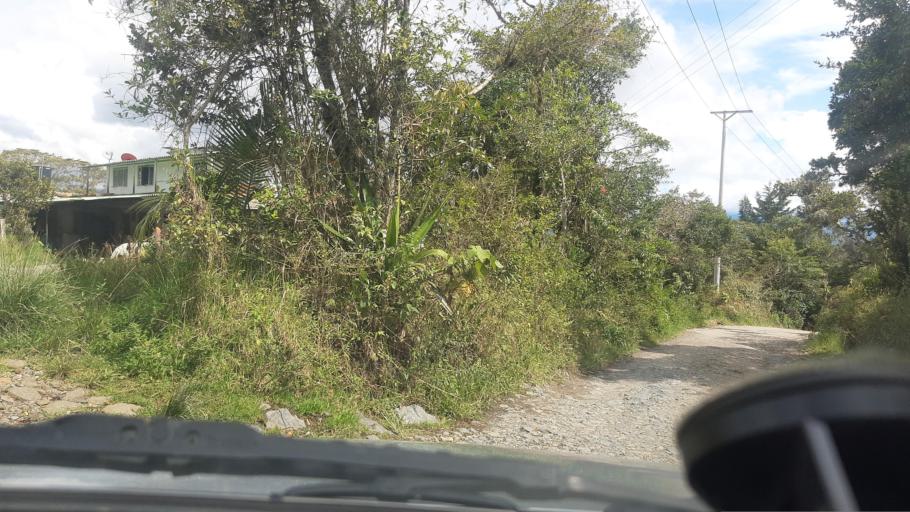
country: CO
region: Boyaca
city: Santa Sofia
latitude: 5.7931
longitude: -73.6052
